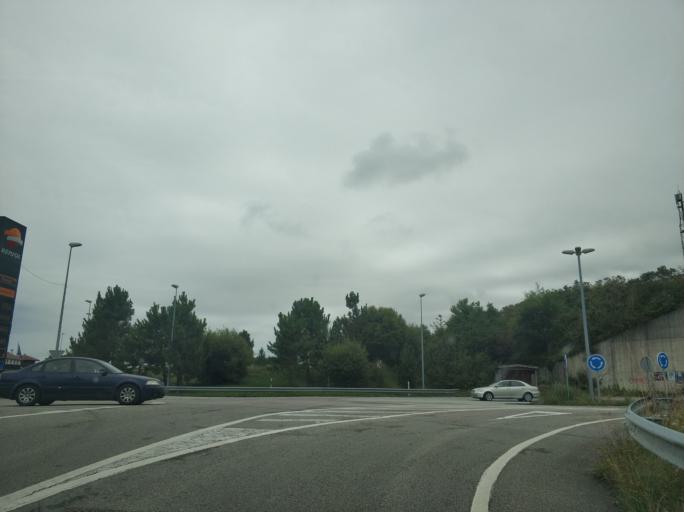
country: ES
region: Asturias
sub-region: Province of Asturias
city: Cudillero
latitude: 43.5574
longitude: -6.2839
